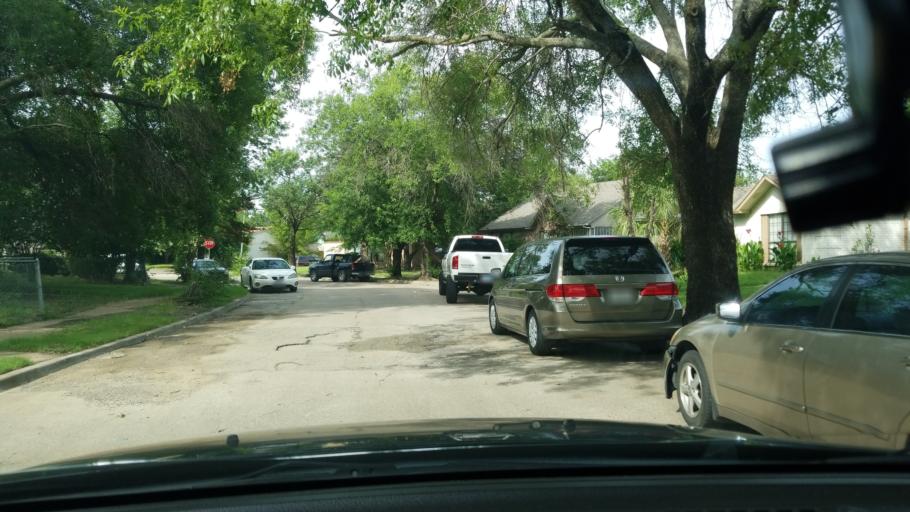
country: US
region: Texas
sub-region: Dallas County
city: Balch Springs
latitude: 32.7667
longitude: -96.6595
